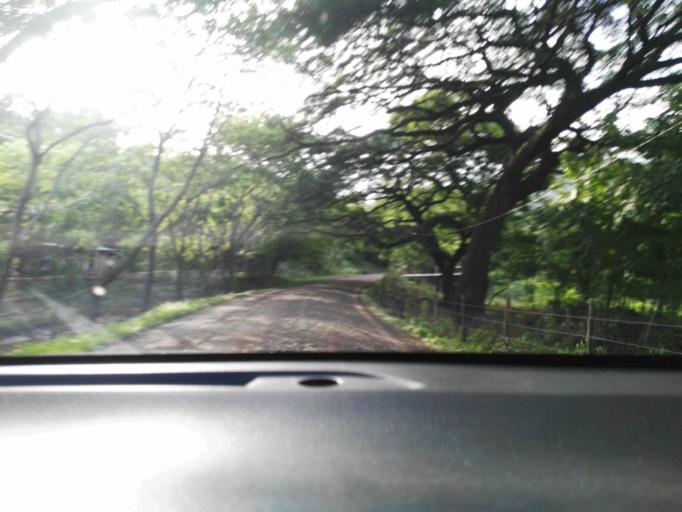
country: NI
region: Matagalpa
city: Terrabona
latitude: 12.8440
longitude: -86.0285
